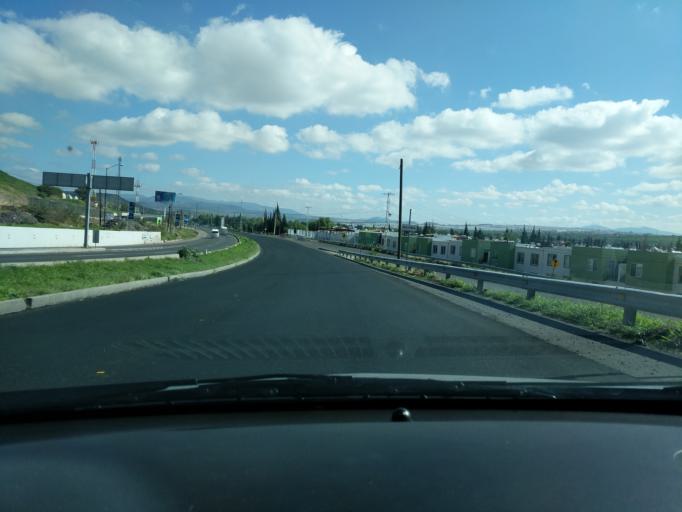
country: MX
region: Guanajuato
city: El Castillo
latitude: 20.6080
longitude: -100.4918
